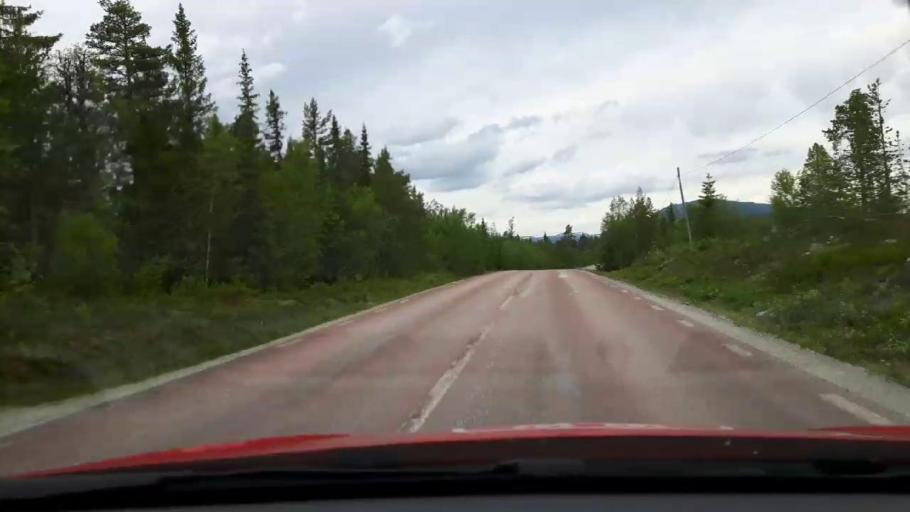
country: NO
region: Hedmark
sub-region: Engerdal
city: Engerdal
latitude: 62.5075
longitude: 12.6131
